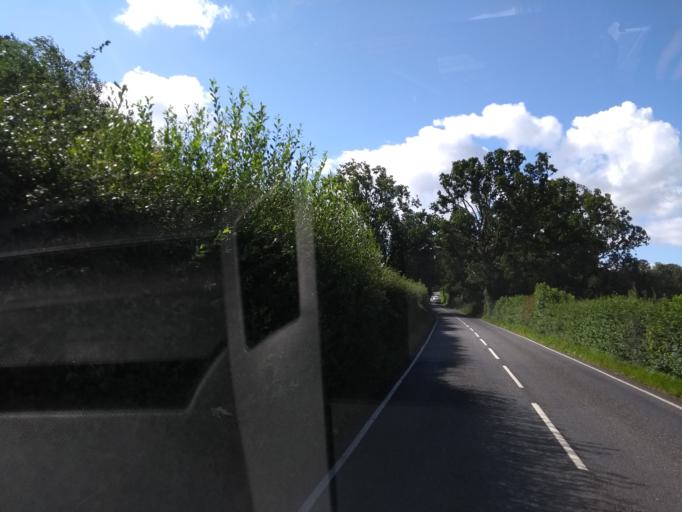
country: GB
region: England
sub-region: Somerset
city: Street
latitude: 51.1184
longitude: -2.7320
